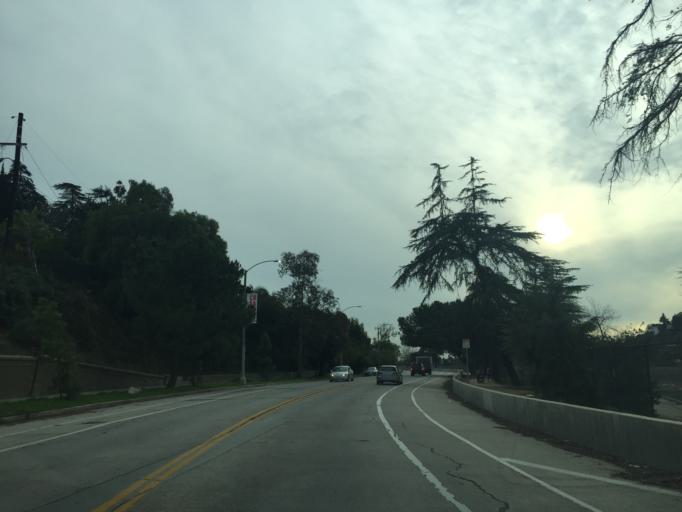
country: US
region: California
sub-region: Los Angeles County
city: Silver Lake
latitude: 34.0951
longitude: -118.2623
